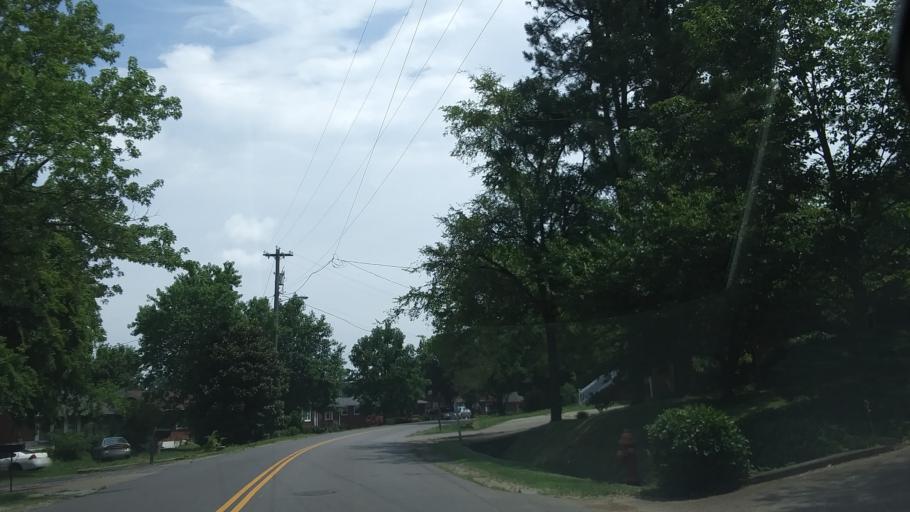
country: US
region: Tennessee
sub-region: Davidson County
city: Belle Meade
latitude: 36.1482
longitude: -86.8793
